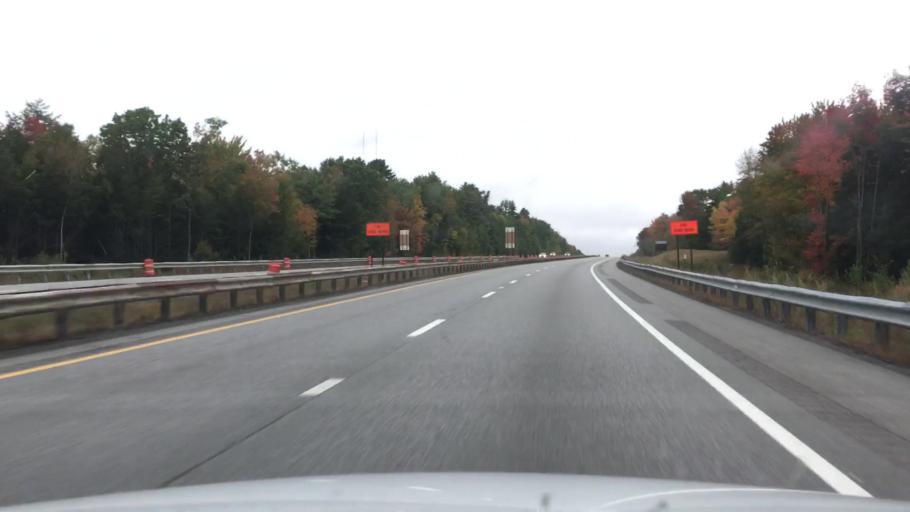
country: US
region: Maine
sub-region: Cumberland County
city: Cumberland Center
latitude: 43.8399
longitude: -70.3246
